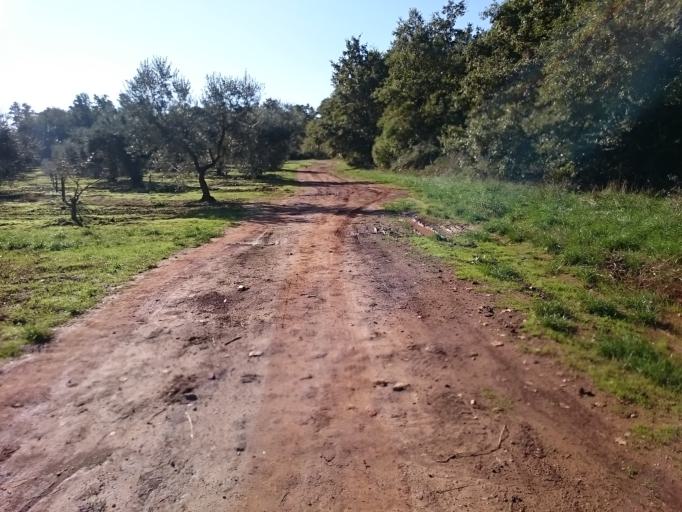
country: HR
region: Istarska
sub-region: Grad Porec
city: Porec
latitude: 45.2689
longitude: 13.5809
